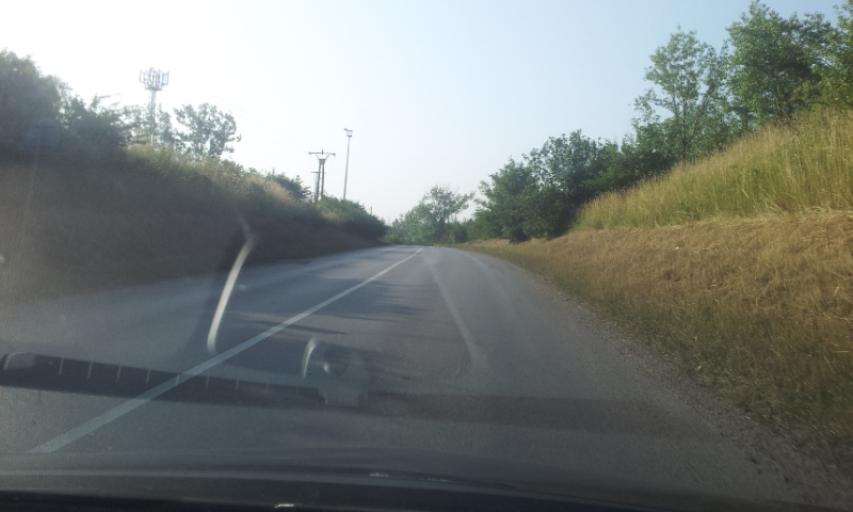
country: SK
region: Kosicky
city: Kosice
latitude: 48.6207
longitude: 21.2290
